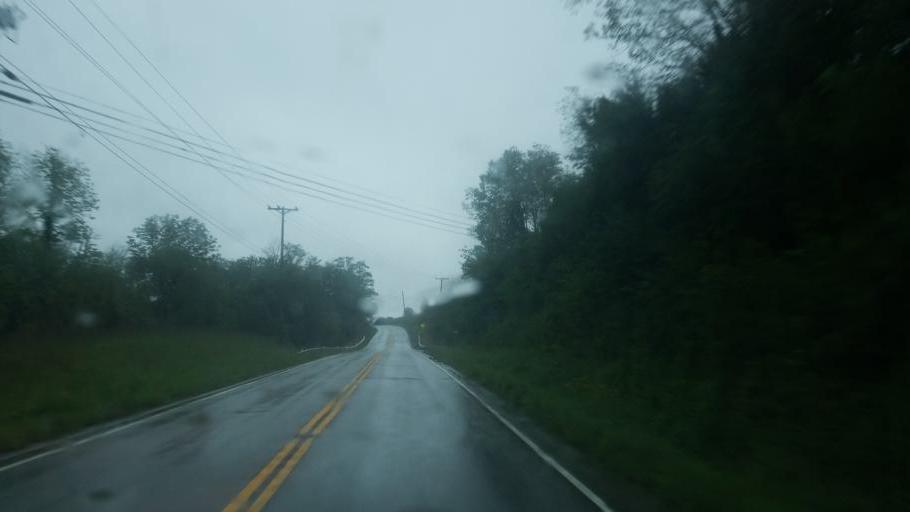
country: US
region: Kentucky
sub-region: Fleming County
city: Flemingsburg
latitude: 38.3607
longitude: -83.6155
